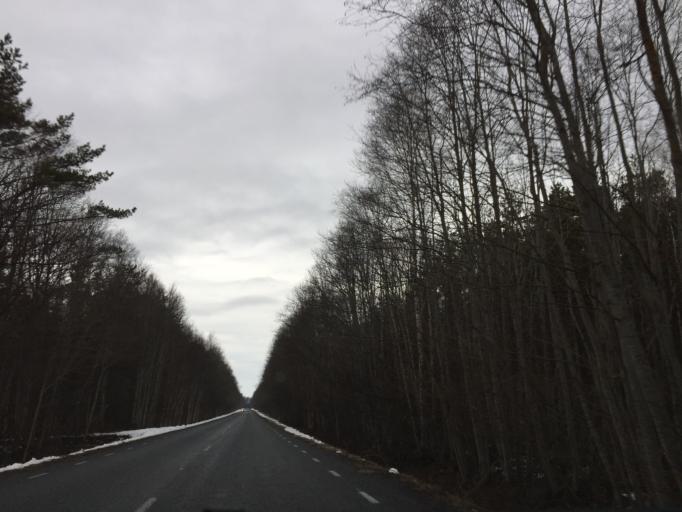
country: EE
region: Saare
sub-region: Orissaare vald
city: Orissaare
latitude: 58.5608
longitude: 22.7732
